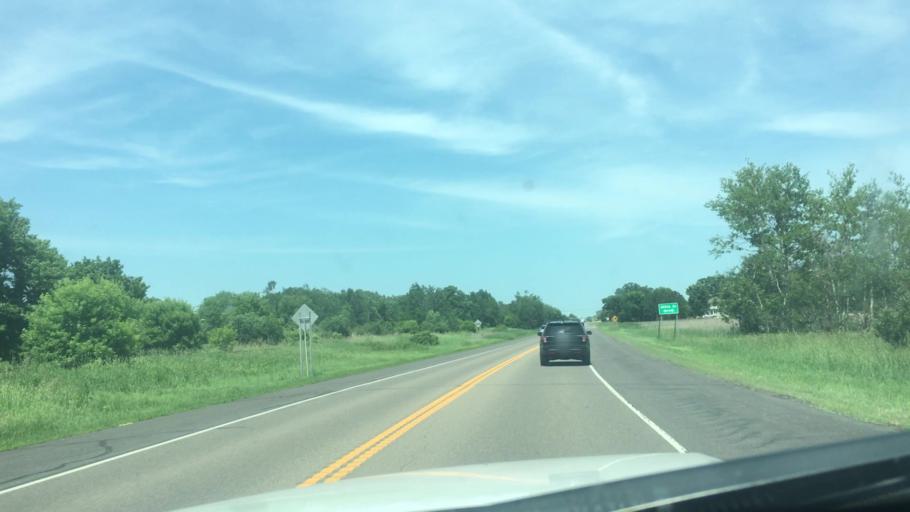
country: US
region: Minnesota
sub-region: Washington County
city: Hugo
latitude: 45.1274
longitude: -93.0027
